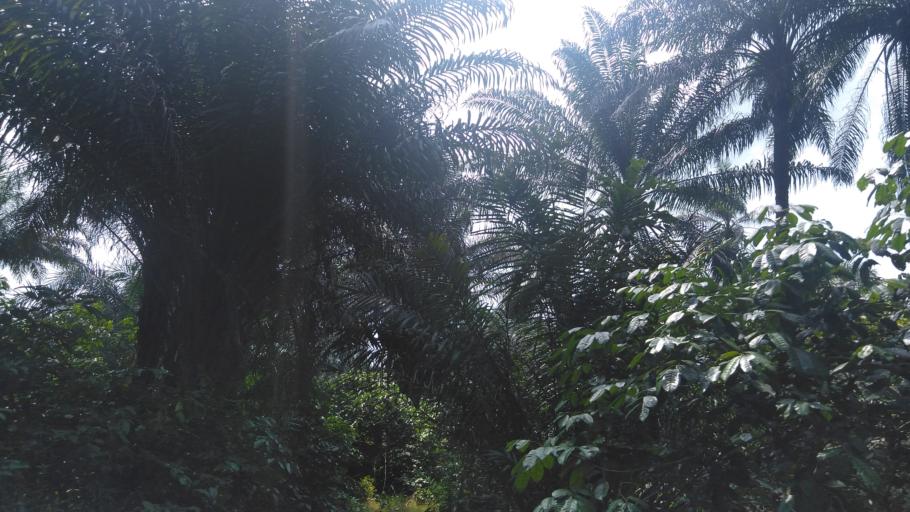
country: NG
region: Abia
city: Aba
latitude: 5.0428
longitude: 7.2379
